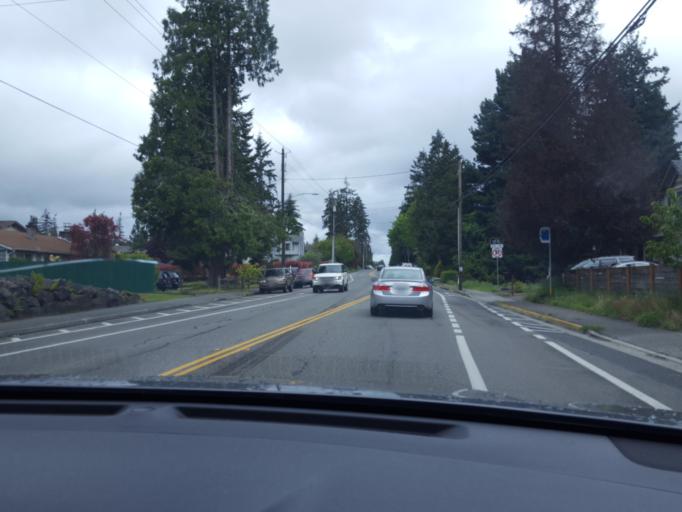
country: US
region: Washington
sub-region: Snohomish County
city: Esperance
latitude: 47.7870
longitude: -122.3355
